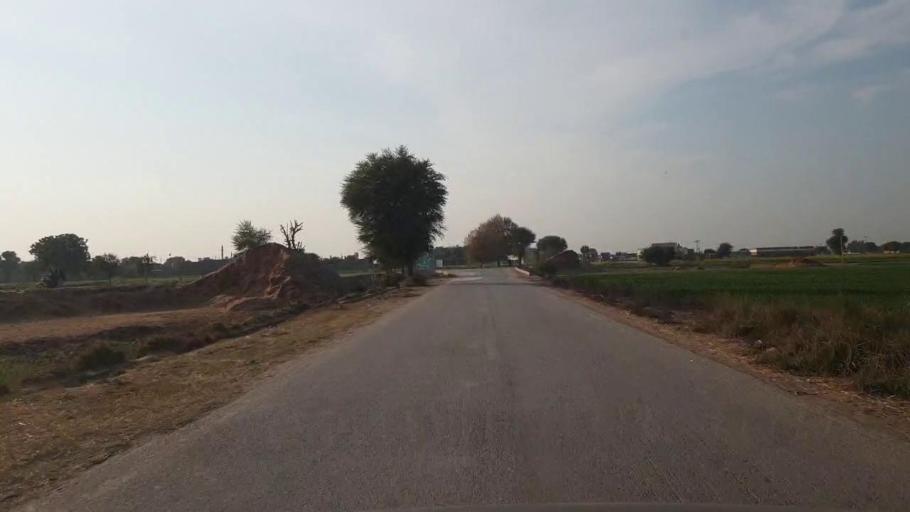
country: PK
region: Sindh
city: Shahpur Chakar
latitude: 26.1635
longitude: 68.6300
